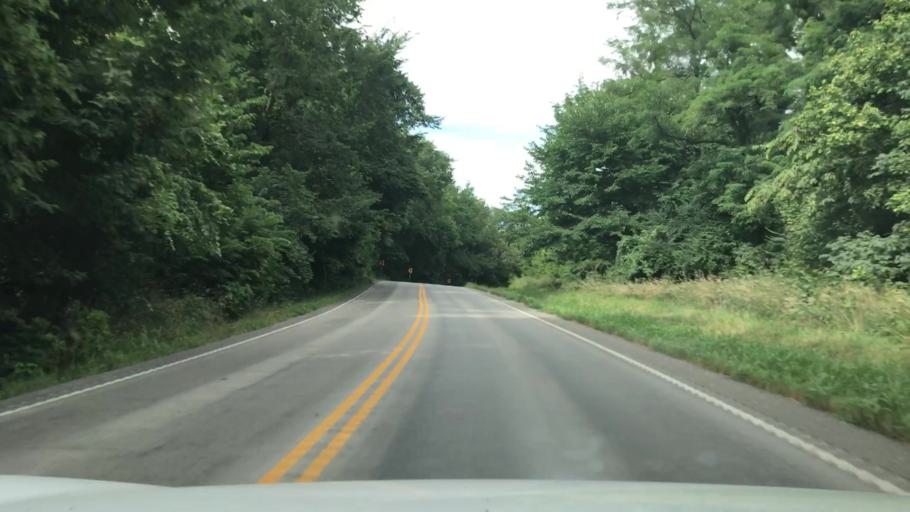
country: US
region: Missouri
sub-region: Saint Charles County
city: Weldon Spring
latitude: 38.6620
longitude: -90.7443
